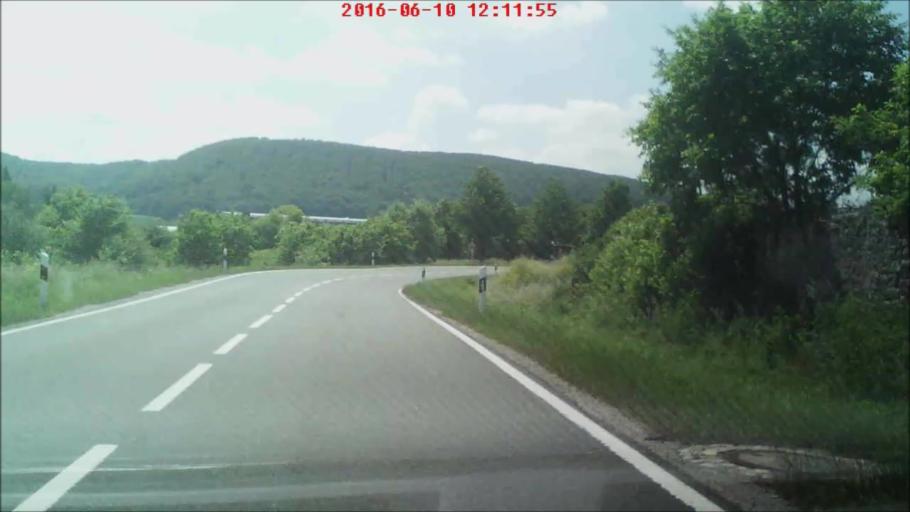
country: DE
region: Thuringia
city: Einhausen
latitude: 50.5348
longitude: 10.4587
